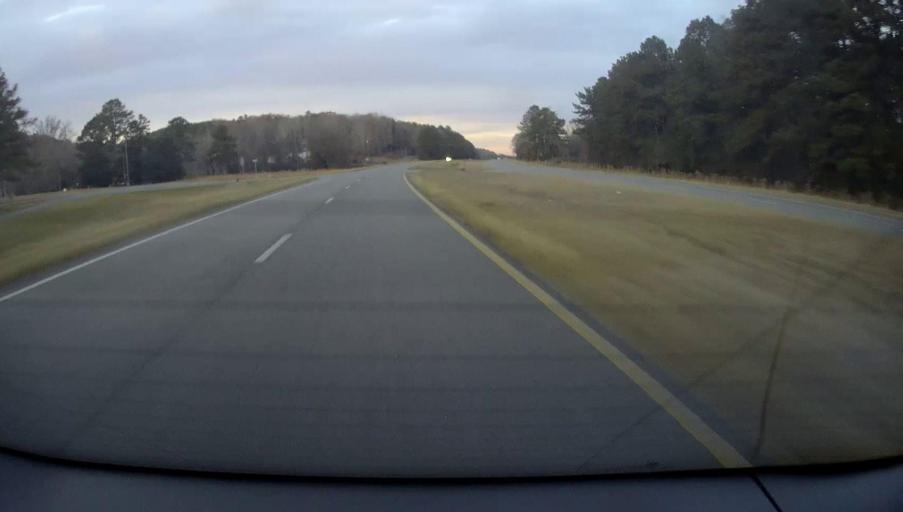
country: US
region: Alabama
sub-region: Etowah County
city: Glencoe
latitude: 33.9147
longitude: -85.9134
